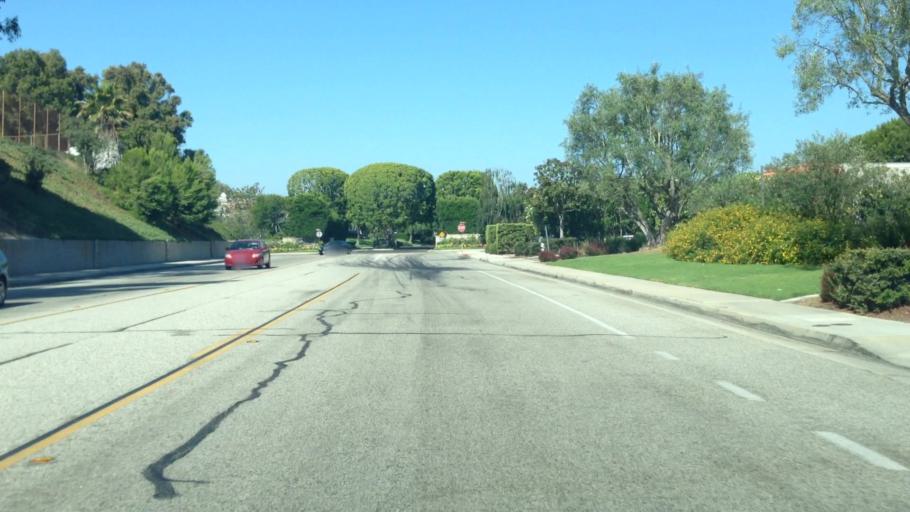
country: US
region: California
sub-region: Los Angeles County
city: Rancho Palos Verdes
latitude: 33.7684
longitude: -118.3794
